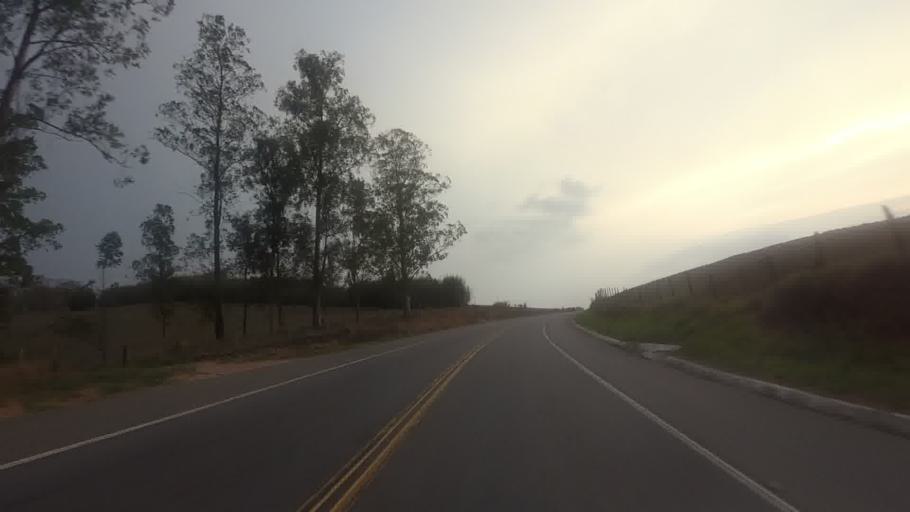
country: BR
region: Rio de Janeiro
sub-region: Carmo
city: Carmo
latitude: -21.8033
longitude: -42.5737
